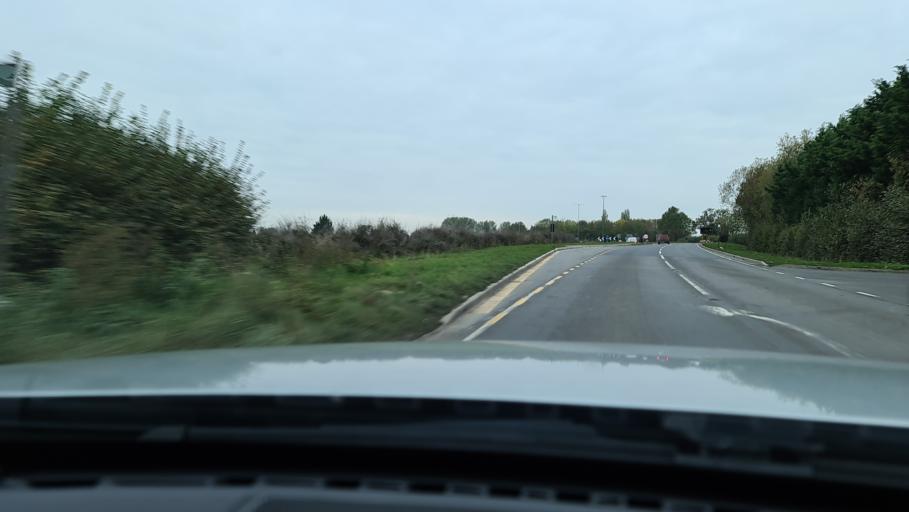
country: GB
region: England
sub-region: Buckinghamshire
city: Waddesdon
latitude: 51.8522
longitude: -0.9584
